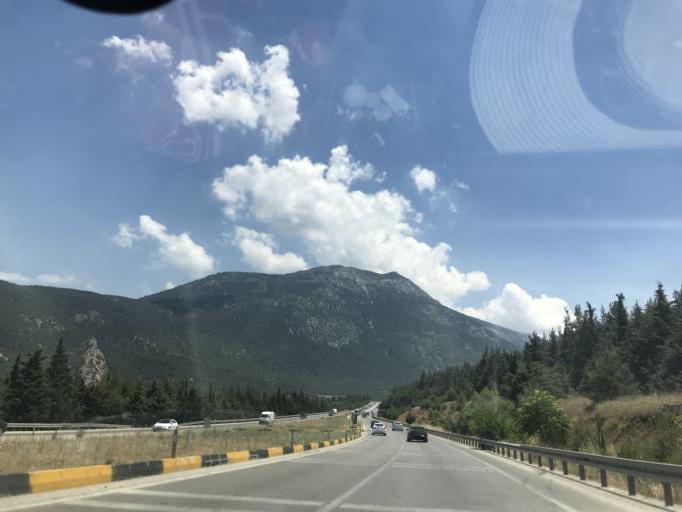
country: TR
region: Denizli
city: Honaz
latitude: 37.7292
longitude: 29.1954
